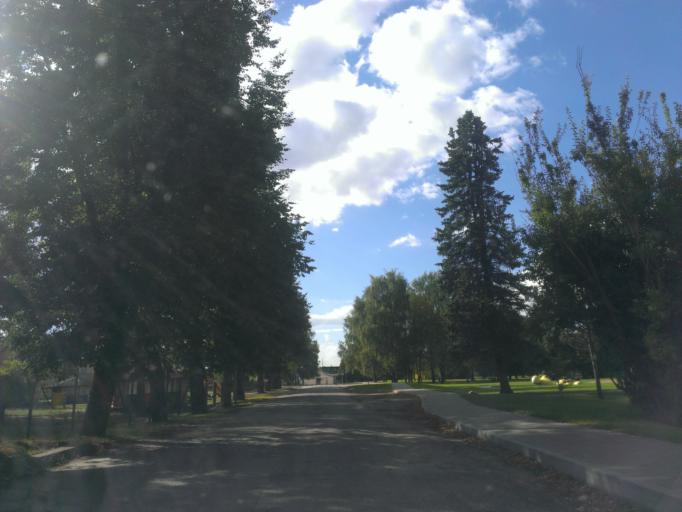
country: LV
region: Sigulda
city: Sigulda
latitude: 57.1490
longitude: 24.8910
